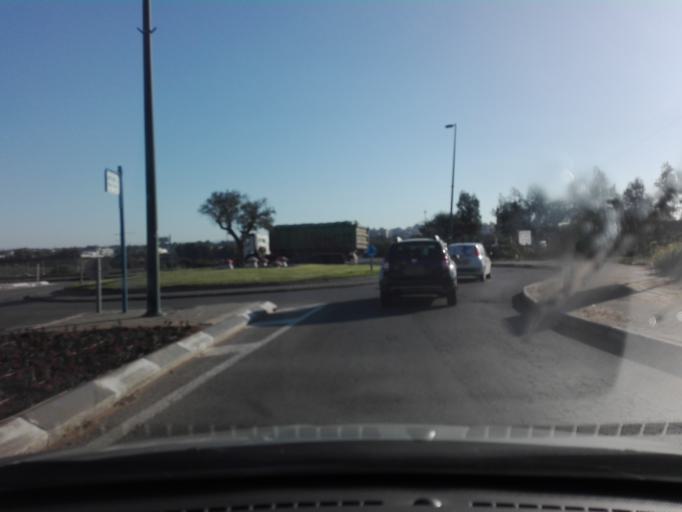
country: IL
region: Central District
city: Netanya
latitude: 32.3085
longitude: 34.8608
